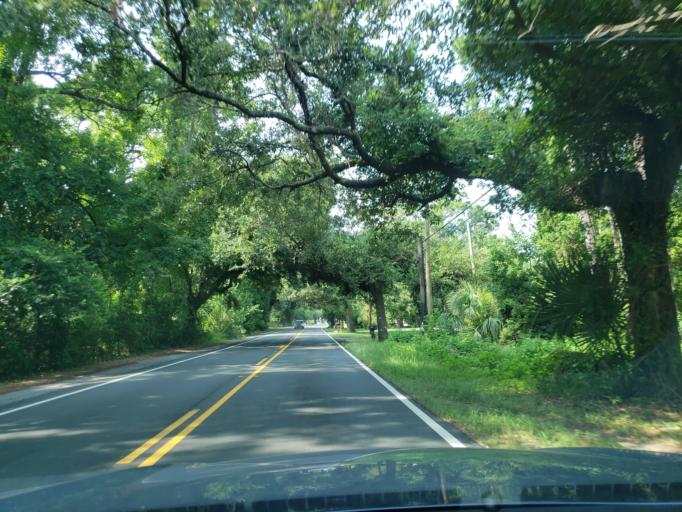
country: US
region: Georgia
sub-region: Chatham County
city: Wilmington Island
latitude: 32.0262
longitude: -80.9658
